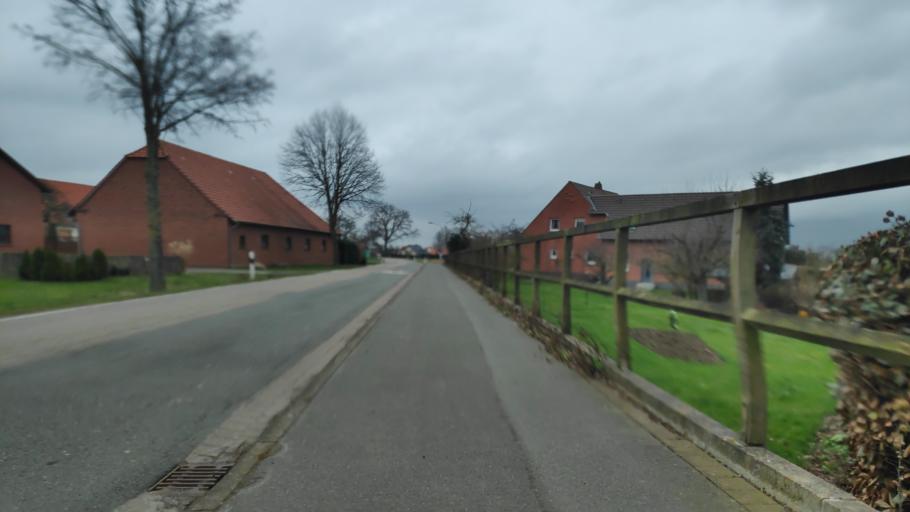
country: DE
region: North Rhine-Westphalia
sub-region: Regierungsbezirk Detmold
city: Hille
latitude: 52.3439
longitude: 8.7961
